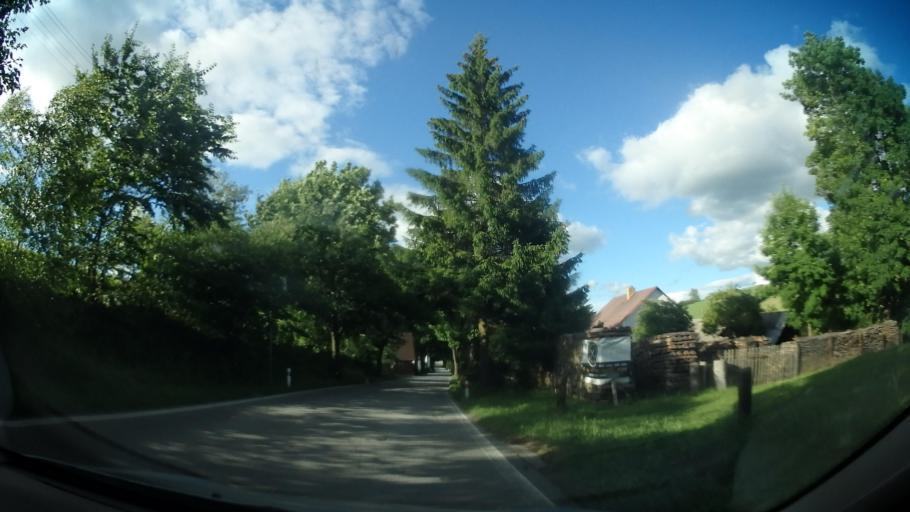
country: CZ
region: Vysocina
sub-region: Okres Zd'ar nad Sazavou
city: Nove Mesto na Morave
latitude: 49.6274
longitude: 16.1114
